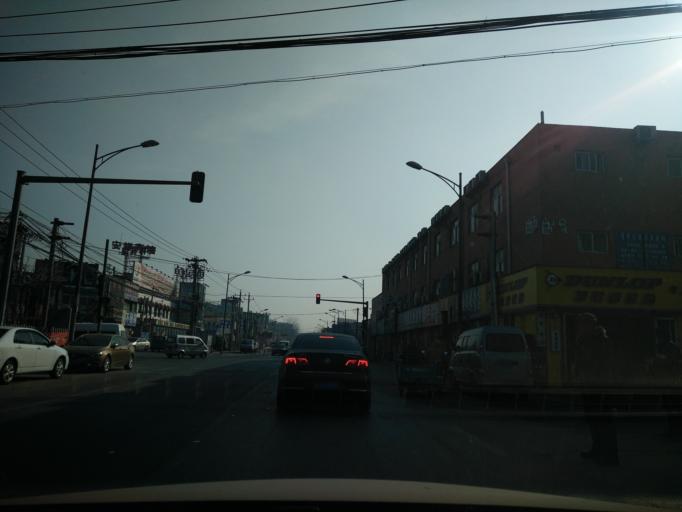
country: CN
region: Beijing
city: Jiugong
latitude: 39.8251
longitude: 116.5019
